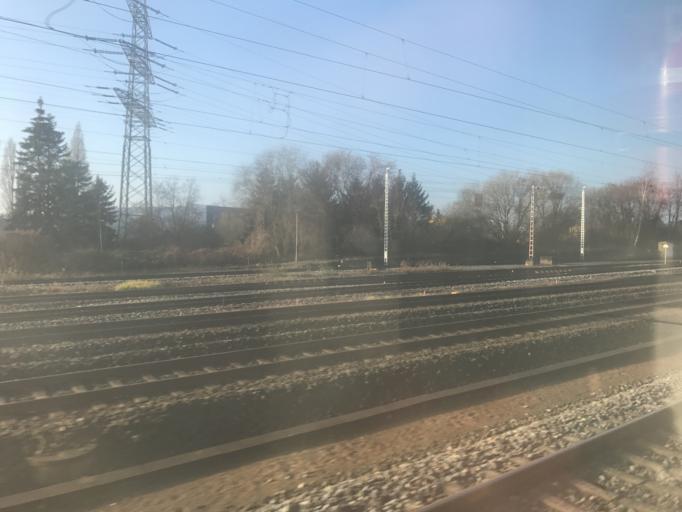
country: DE
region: North Rhine-Westphalia
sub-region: Regierungsbezirk Dusseldorf
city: Erkrath
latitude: 51.1876
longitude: 6.8542
